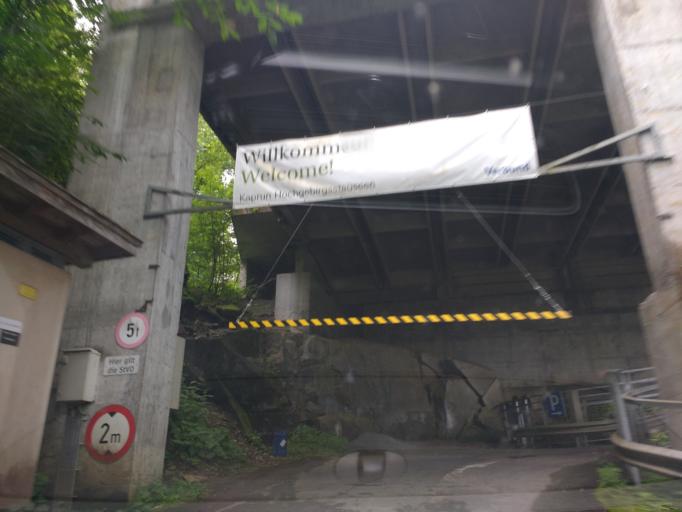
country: AT
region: Salzburg
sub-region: Politischer Bezirk Zell am See
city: Kaprun
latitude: 47.2173
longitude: 12.7262
